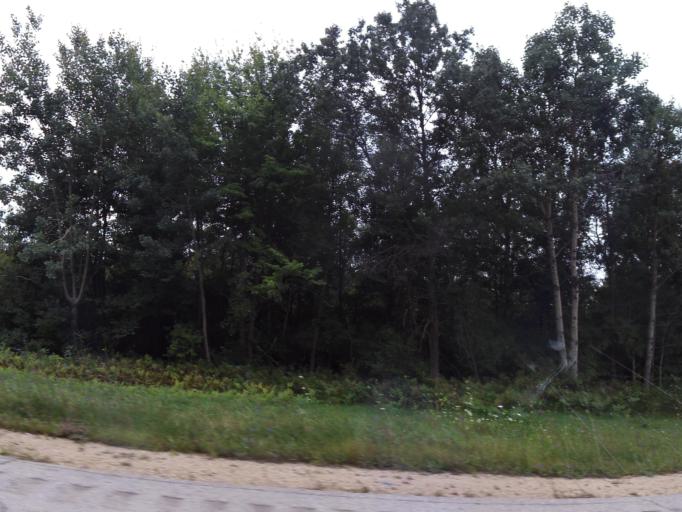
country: US
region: Wisconsin
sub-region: Monroe County
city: Sparta
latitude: 43.9433
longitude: -90.7550
